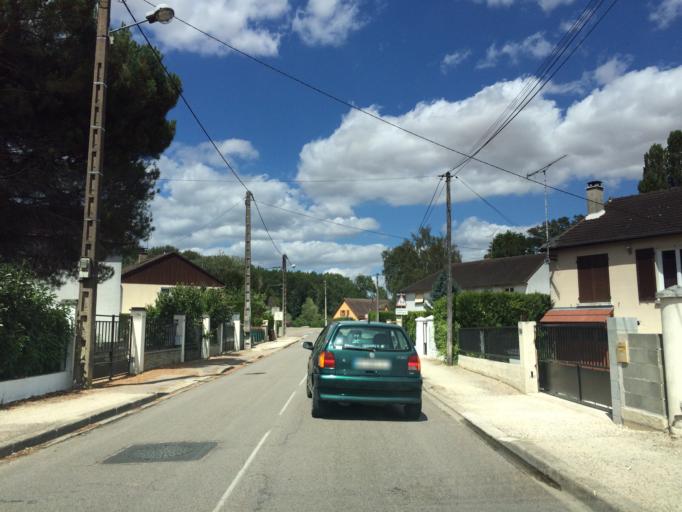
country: FR
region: Bourgogne
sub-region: Departement de l'Yonne
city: Laroche-Saint-Cydroine
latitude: 47.9554
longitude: 3.4997
